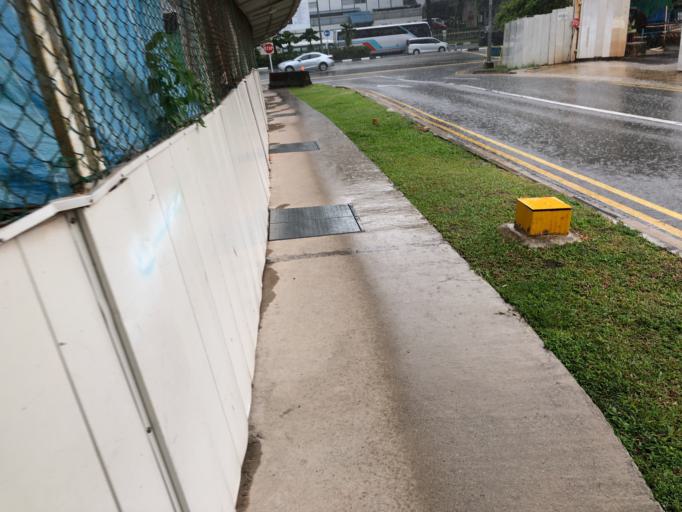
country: SG
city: Singapore
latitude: 1.2826
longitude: 103.8378
